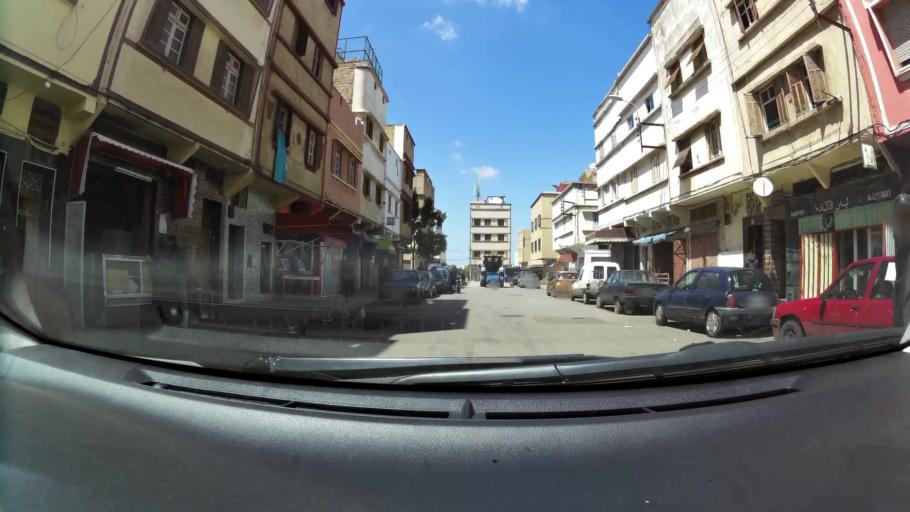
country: MA
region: Grand Casablanca
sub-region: Casablanca
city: Casablanca
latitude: 33.5597
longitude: -7.5831
